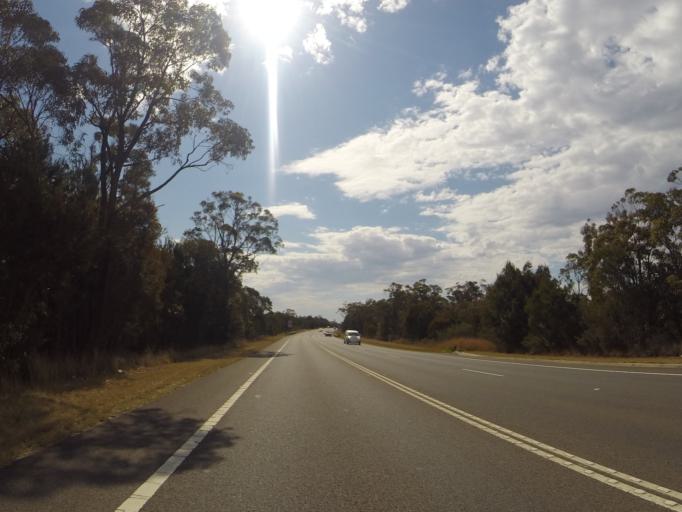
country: AU
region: New South Wales
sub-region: Liverpool
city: Holsworthy
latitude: -34.0362
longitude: 150.9603
